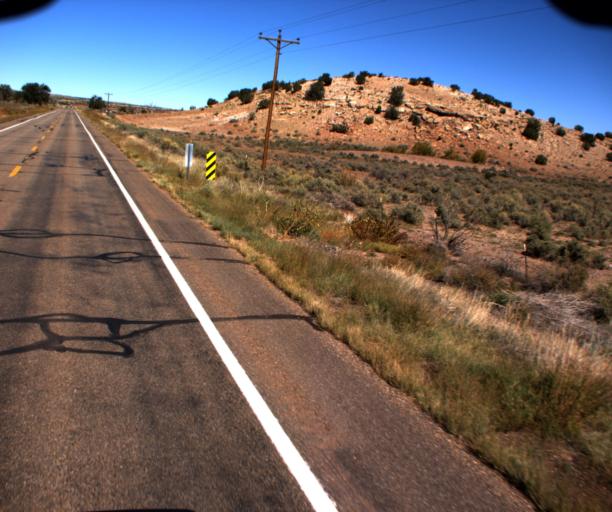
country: US
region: Arizona
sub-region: Apache County
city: Saint Johns
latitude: 34.4284
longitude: -109.4106
